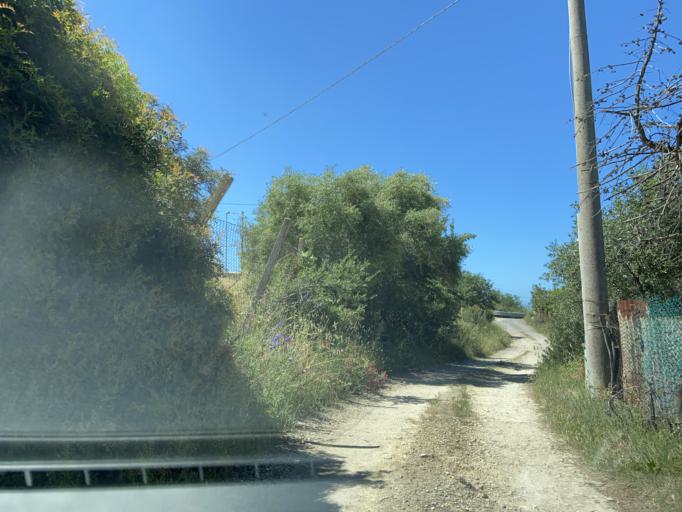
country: IT
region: Latium
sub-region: Citta metropolitana di Roma Capitale
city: Civitavecchia
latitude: 42.0877
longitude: 11.8292
